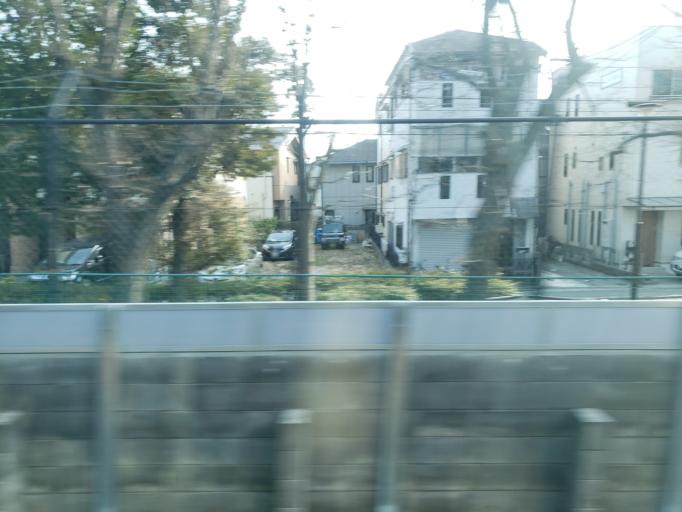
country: JP
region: Hyogo
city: Nishinomiya-hama
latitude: 34.7389
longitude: 135.3674
